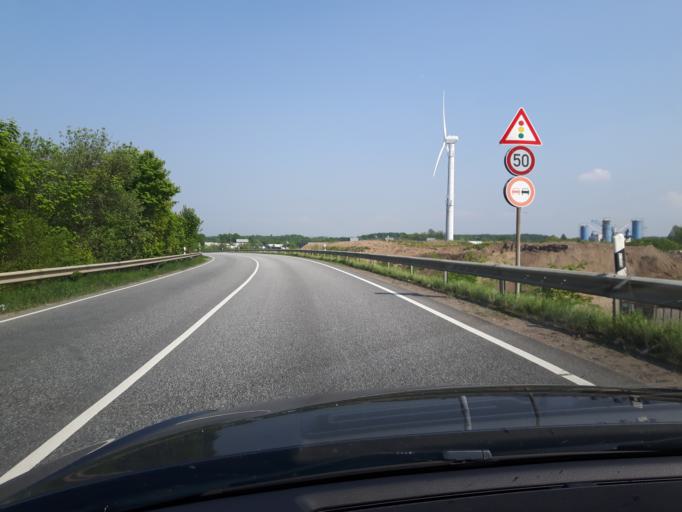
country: DE
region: Schleswig-Holstein
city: Travemuende
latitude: 53.9330
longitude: 10.8370
